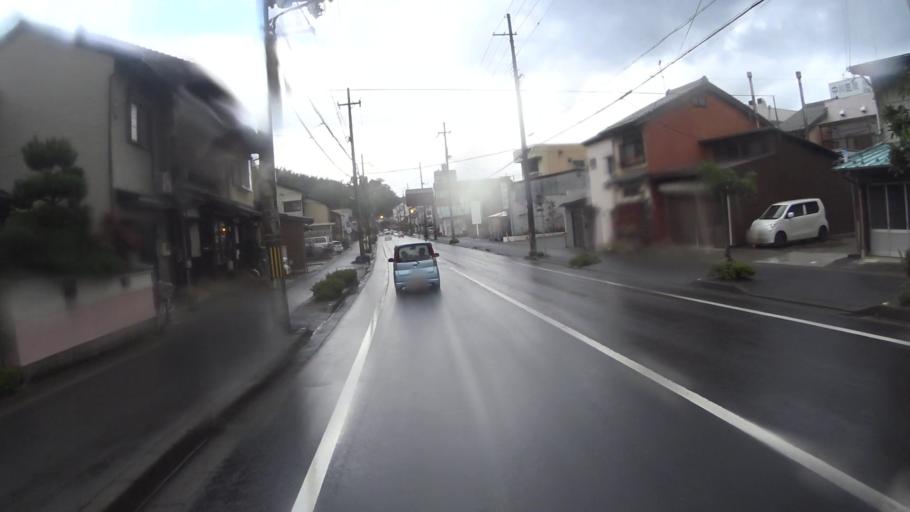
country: JP
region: Kyoto
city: Miyazu
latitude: 35.5404
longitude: 135.1901
